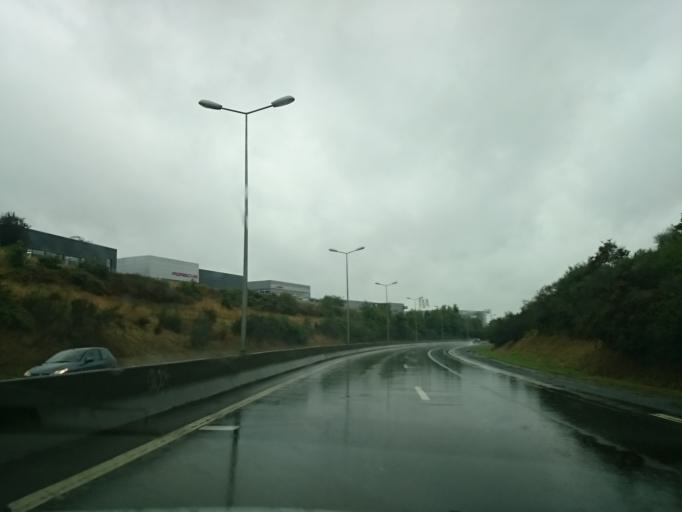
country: FR
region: Brittany
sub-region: Departement d'Ille-et-Vilaine
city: Chantepie
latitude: 48.1046
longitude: -1.6143
